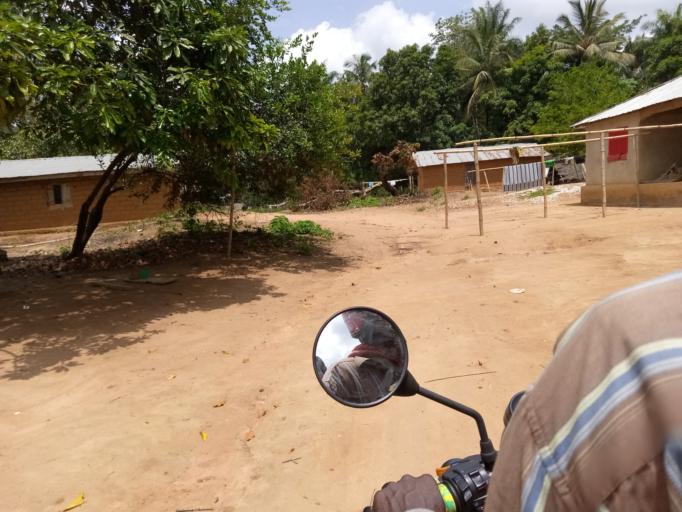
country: SL
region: Western Area
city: Waterloo
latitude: 8.4031
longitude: -13.0250
